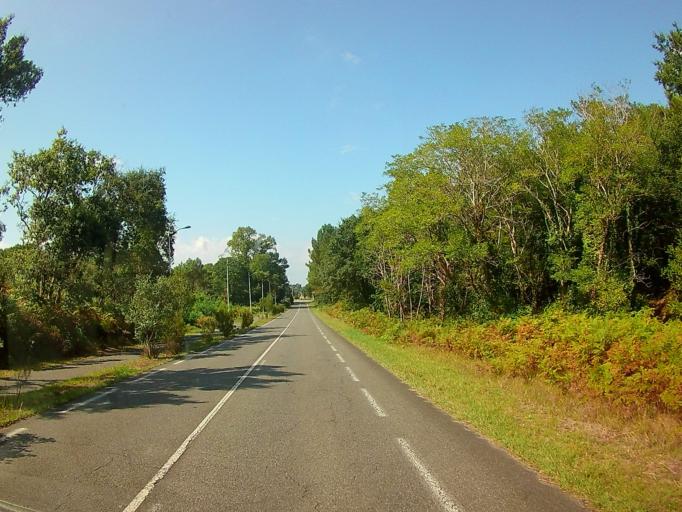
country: FR
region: Aquitaine
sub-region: Departement des Landes
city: Labenne
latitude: 43.5903
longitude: -1.4442
